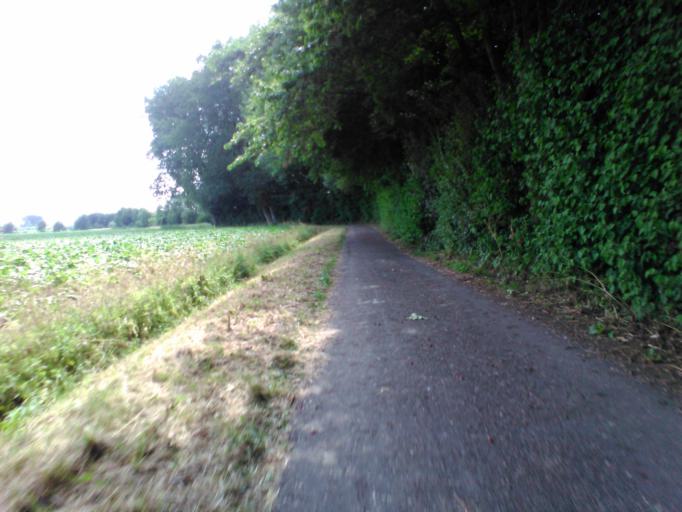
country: NL
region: North Brabant
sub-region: Gemeente Woudrichem
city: Woudrichem
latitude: 51.7839
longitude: 4.9924
